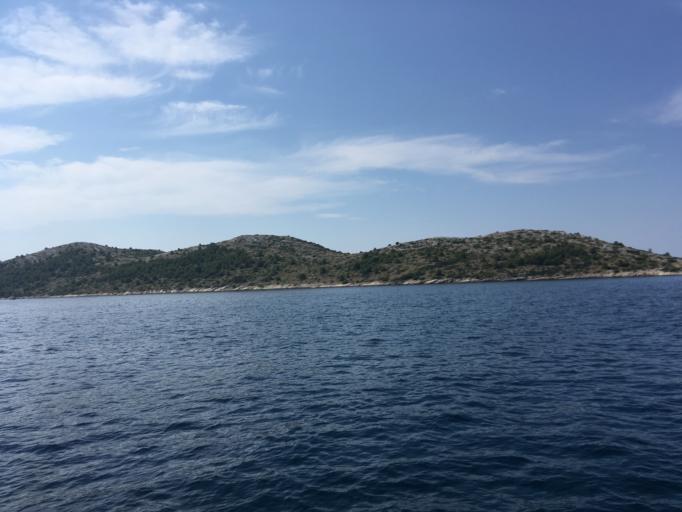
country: HR
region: Zadarska
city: Sali
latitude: 43.8367
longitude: 15.2373
